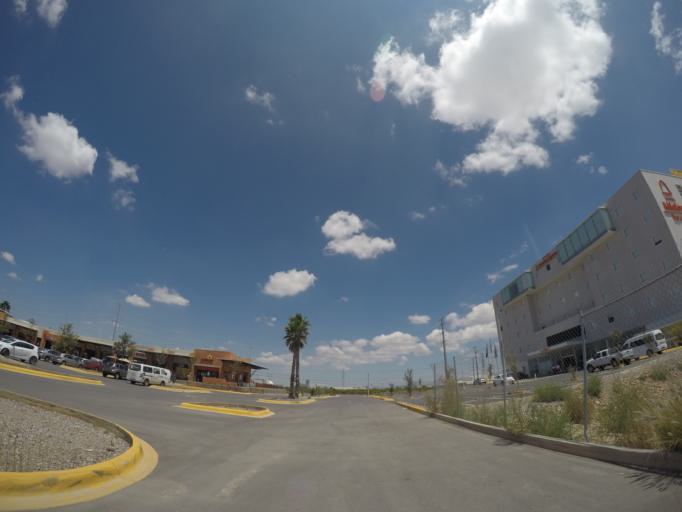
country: MX
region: San Luis Potosi
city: La Pila
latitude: 22.0409
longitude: -100.8926
